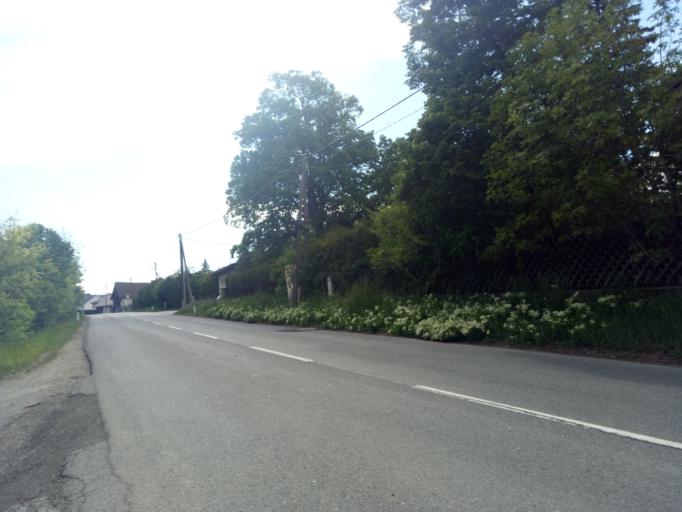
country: AT
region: Lower Austria
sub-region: Politischer Bezirk Wien-Umgebung
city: Wolfsgraben
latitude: 48.1367
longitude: 16.1259
